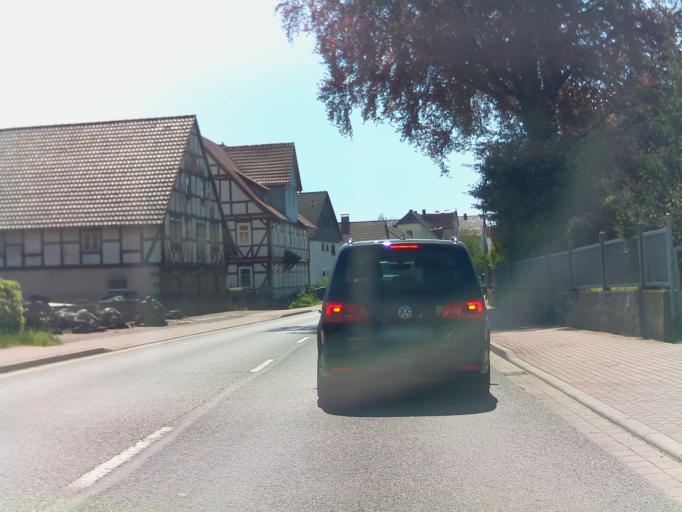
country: DE
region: Hesse
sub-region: Regierungsbezirk Kassel
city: Niederaula
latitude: 50.8031
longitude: 9.6124
